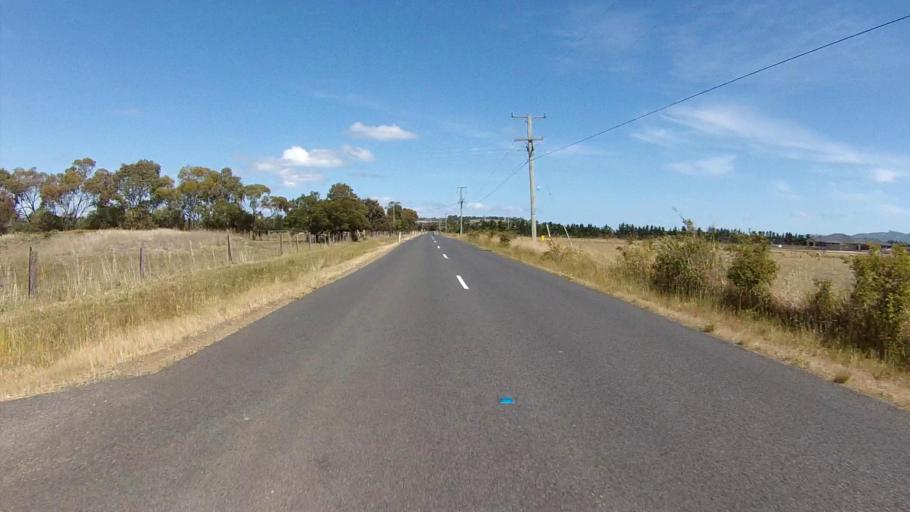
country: AU
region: Tasmania
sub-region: Sorell
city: Sorell
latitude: -42.7745
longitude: 147.5194
